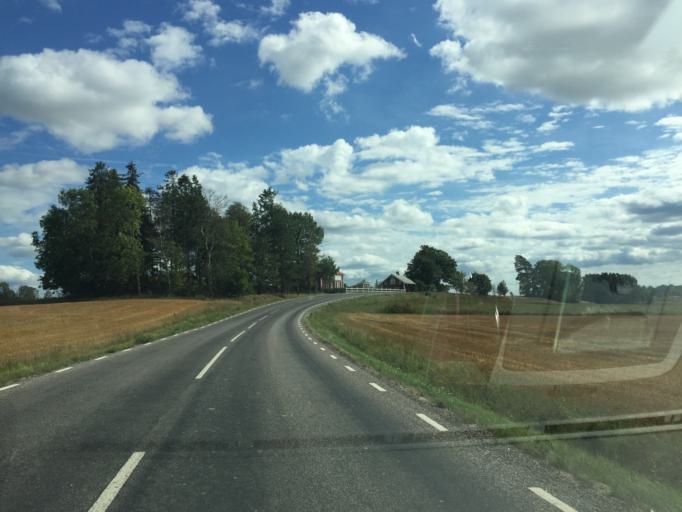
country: SE
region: OErebro
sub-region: Hallsbergs Kommun
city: Hallsberg
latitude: 59.1168
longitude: 15.0087
